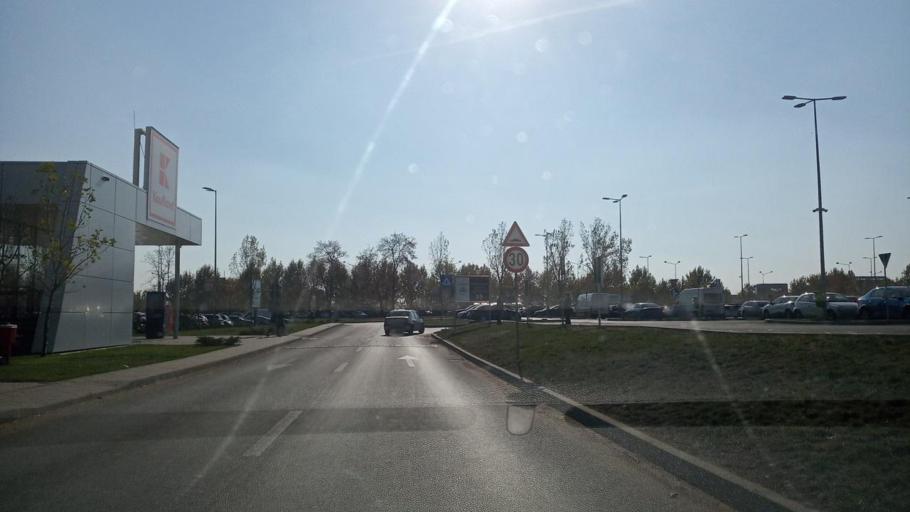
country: RO
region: Ilfov
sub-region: Comuna Glina
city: Catelu
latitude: 44.4088
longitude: 26.1963
